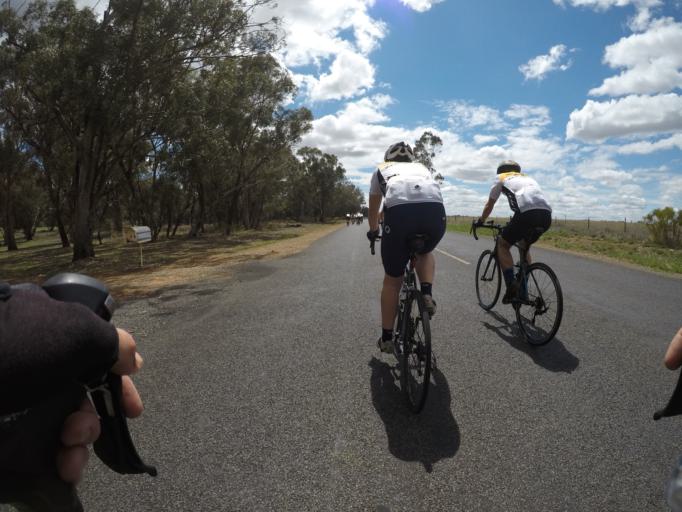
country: AU
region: New South Wales
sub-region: Dubbo Municipality
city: Dubbo
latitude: -32.4585
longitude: 148.5753
